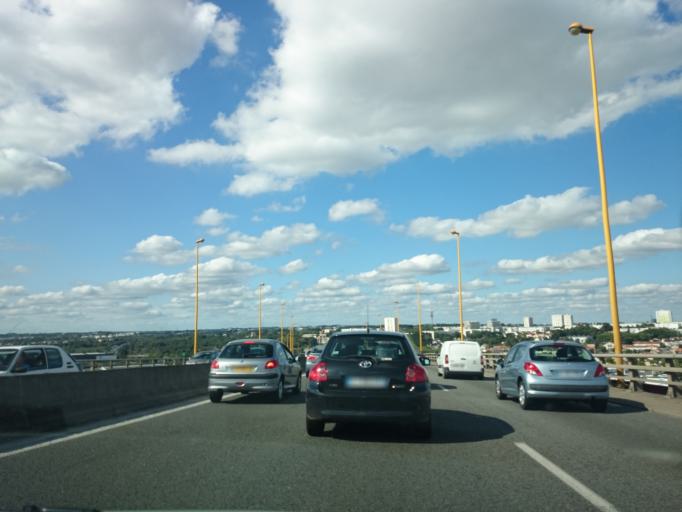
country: FR
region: Pays de la Loire
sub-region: Departement de la Loire-Atlantique
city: Bouguenais
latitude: 47.1945
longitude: -1.6136
